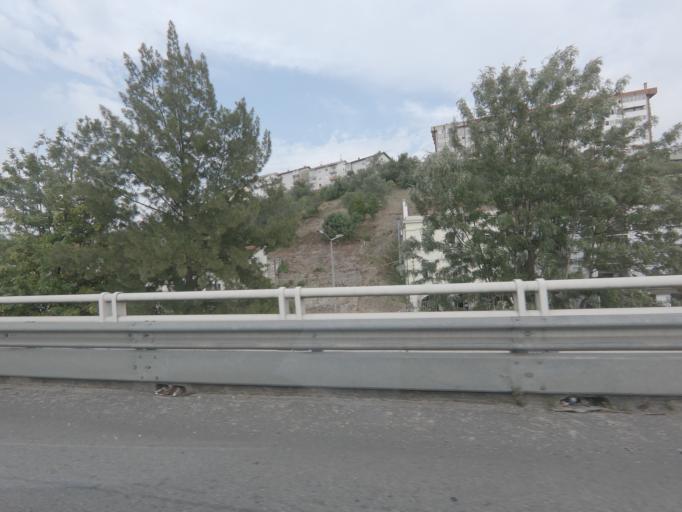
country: PT
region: Coimbra
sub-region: Coimbra
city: Coimbra
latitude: 40.2222
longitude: -8.4396
